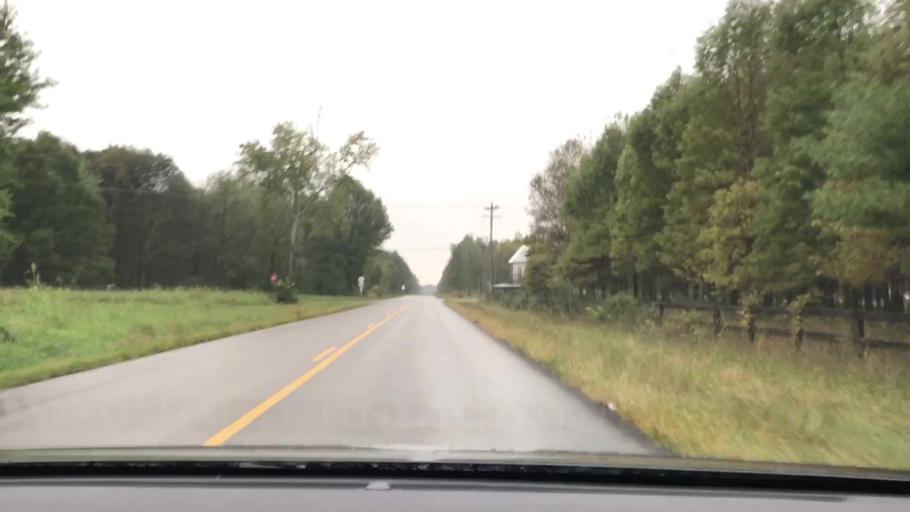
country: US
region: Kentucky
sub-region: Hopkins County
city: Madisonville
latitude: 37.3624
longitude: -87.3745
